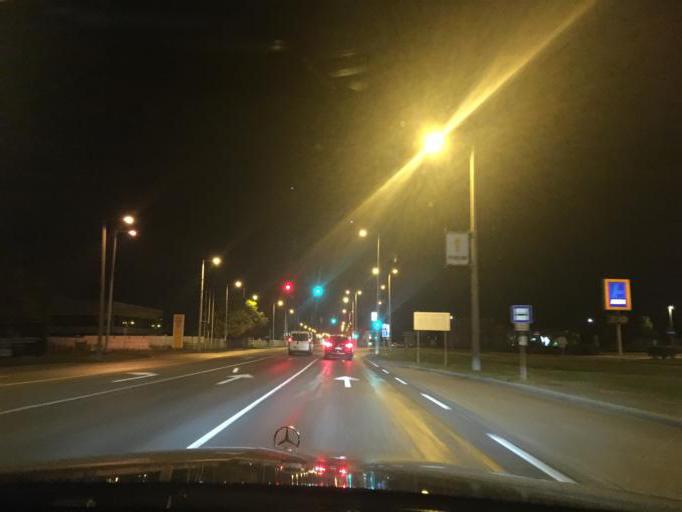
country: HU
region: Hajdu-Bihar
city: Debrecen
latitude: 47.4945
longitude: 21.6320
